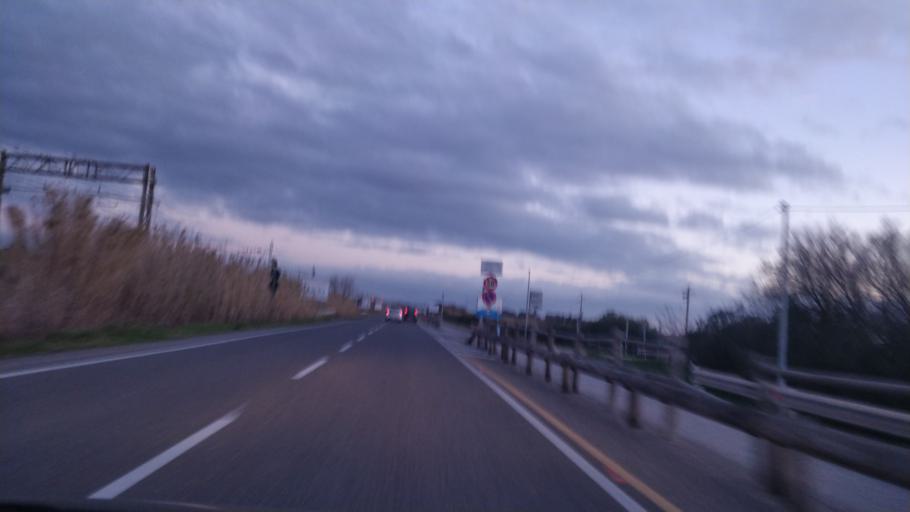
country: IT
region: Tuscany
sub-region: Provincia di Livorno
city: Rosignano Solvay-Castiglioncello
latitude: 43.3767
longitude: 10.4467
